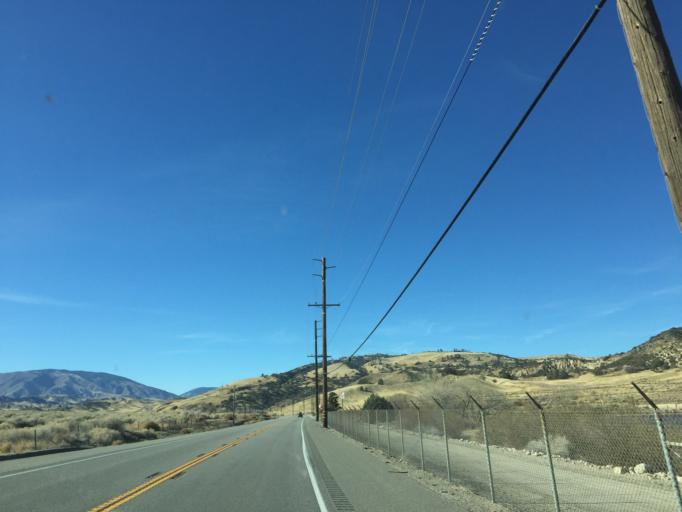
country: US
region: California
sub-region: Kern County
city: Lebec
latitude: 34.7705
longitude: -118.7564
